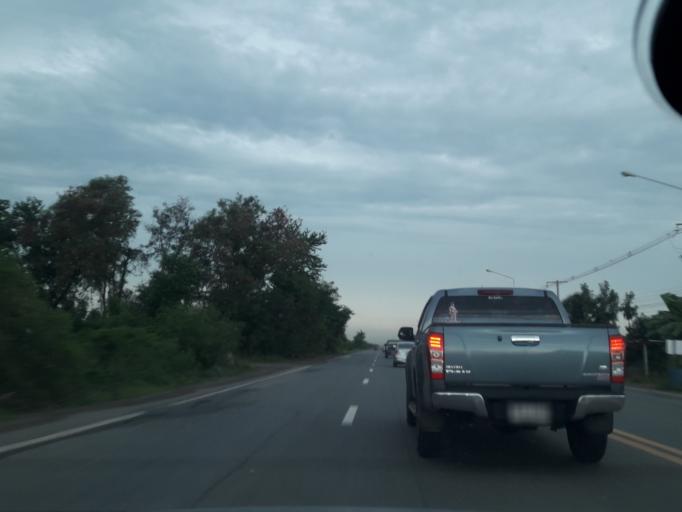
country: TH
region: Pathum Thani
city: Ban Rangsit
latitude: 14.0955
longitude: 100.7472
